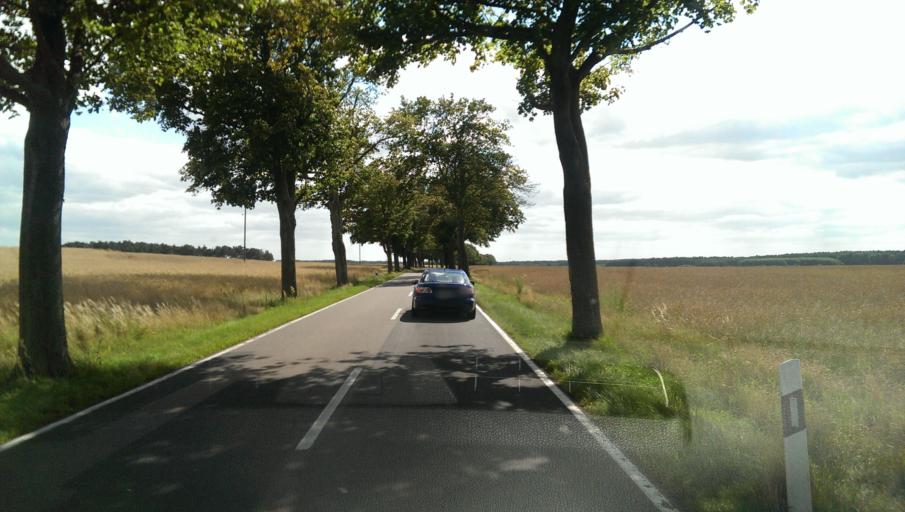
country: DE
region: Saxony-Anhalt
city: Nudersdorf
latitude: 52.0058
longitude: 12.5944
